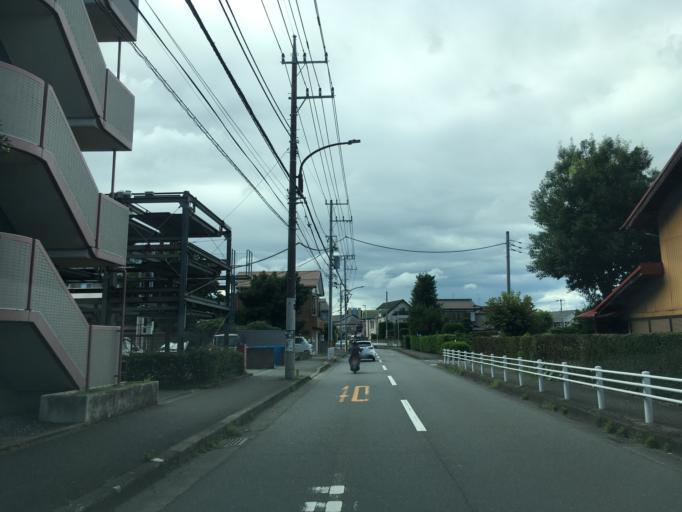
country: JP
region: Tokyo
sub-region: Machida-shi
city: Machida
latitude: 35.5598
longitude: 139.4098
